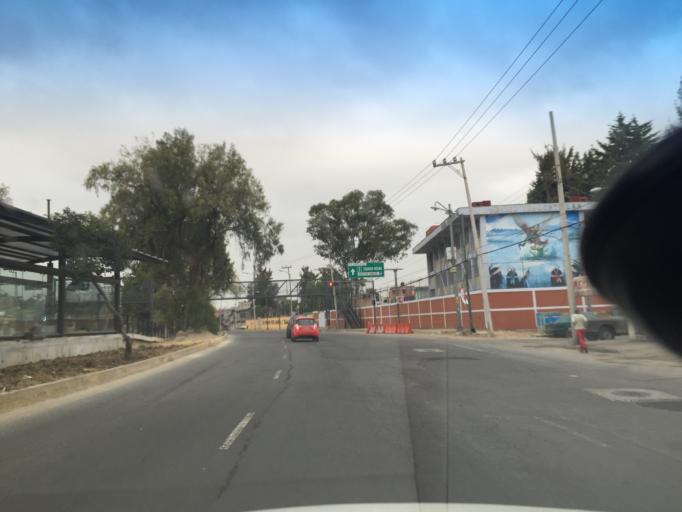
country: MX
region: Mexico City
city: Venustiano Carranza
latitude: 19.4670
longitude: -99.0754
